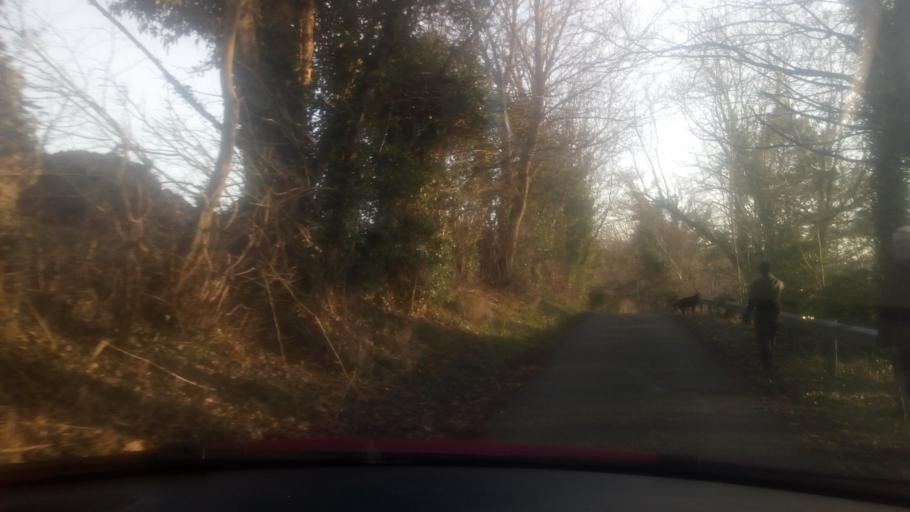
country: GB
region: Scotland
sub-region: The Scottish Borders
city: Jedburgh
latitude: 55.4924
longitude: -2.5417
